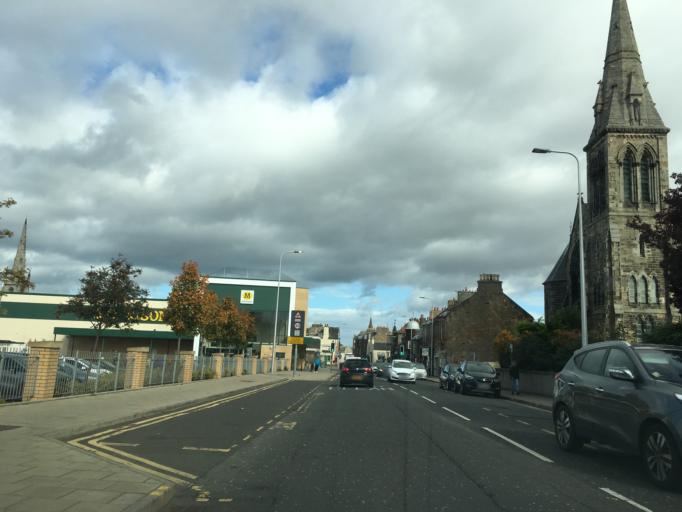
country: GB
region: Scotland
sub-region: Midlothian
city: Dalkeith
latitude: 55.8918
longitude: -3.0742
